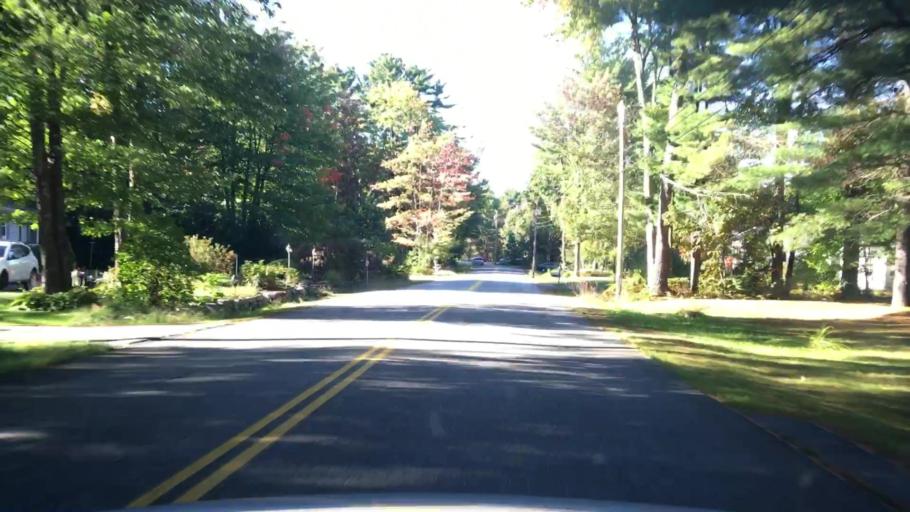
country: US
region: Maine
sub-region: Androscoggin County
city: Sabattus
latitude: 44.0745
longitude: -70.1450
